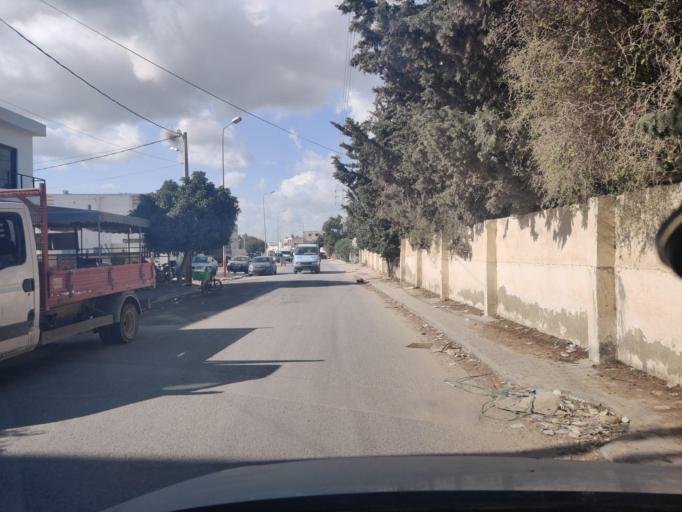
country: TN
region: Tunis
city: Al Marsa
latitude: 36.8826
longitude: 10.2750
